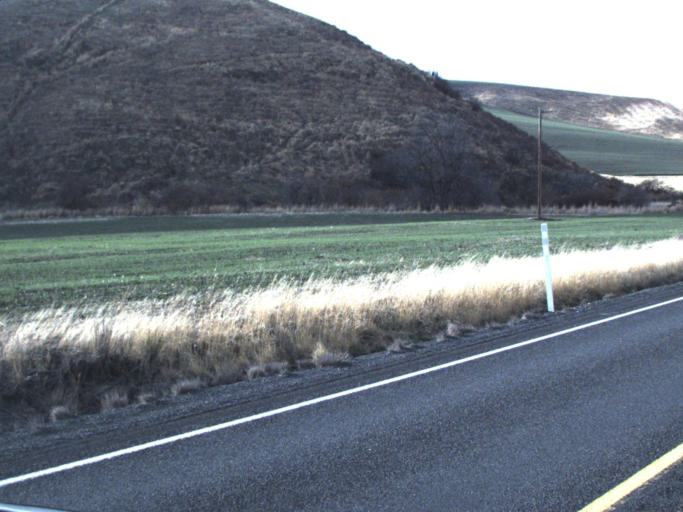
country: US
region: Washington
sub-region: Garfield County
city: Pomeroy
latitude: 46.5047
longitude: -117.7790
